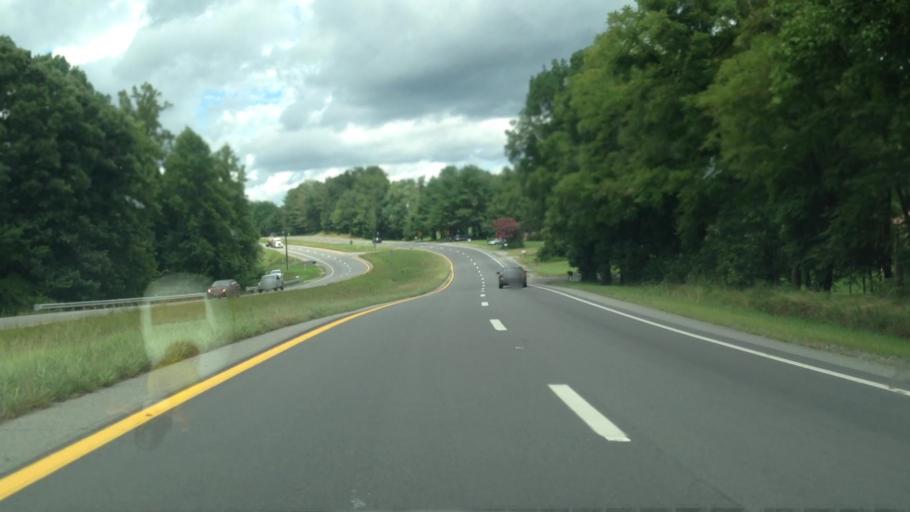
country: US
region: Virginia
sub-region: Henry County
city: Stanleytown
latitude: 36.8004
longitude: -79.9376
